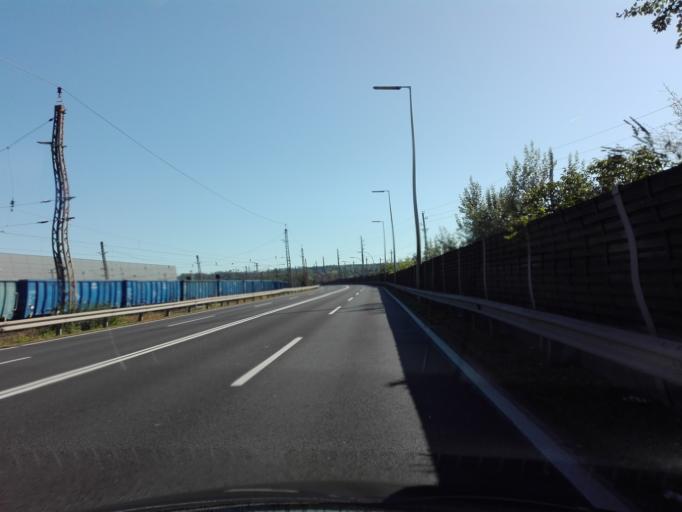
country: AT
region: Upper Austria
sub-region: Politischer Bezirk Urfahr-Umgebung
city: Steyregg
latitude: 48.2625
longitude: 14.3242
